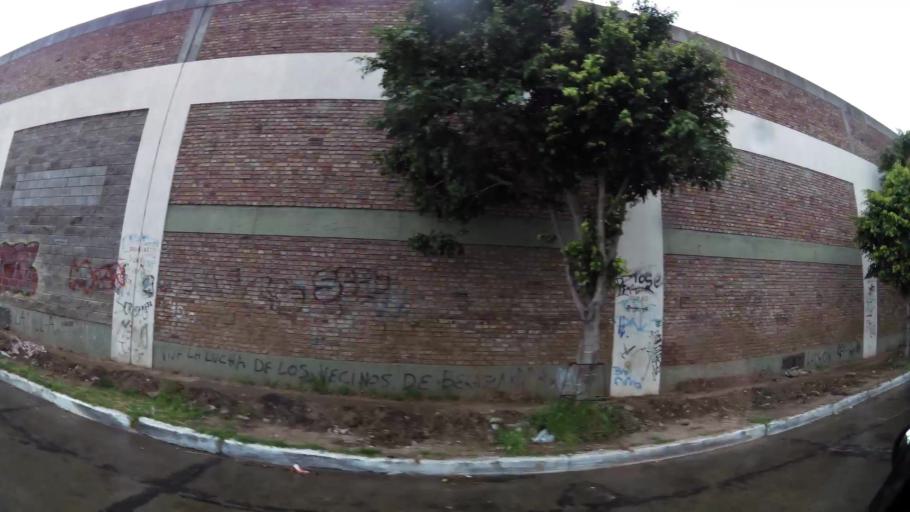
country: AR
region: Buenos Aires
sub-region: Partido de Quilmes
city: Quilmes
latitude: -34.7654
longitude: -58.2106
